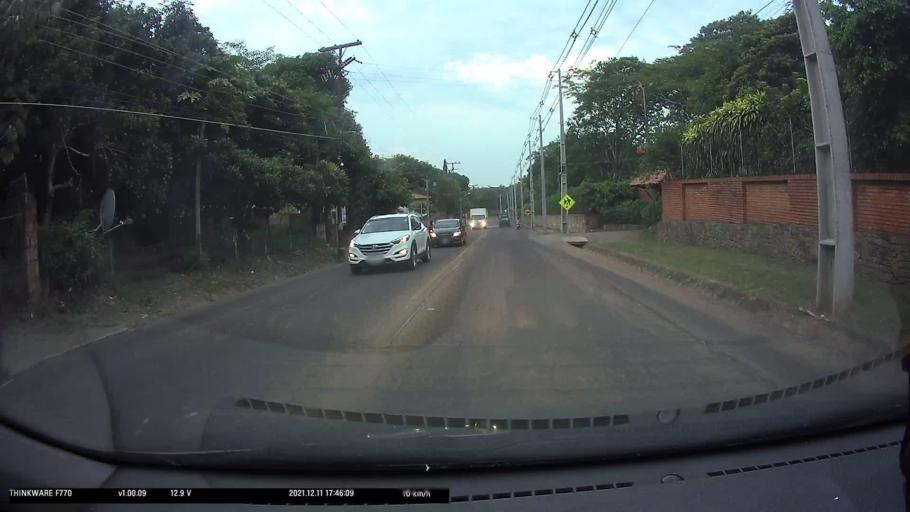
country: PY
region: Cordillera
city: San Bernardino
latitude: -25.2965
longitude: -57.2811
